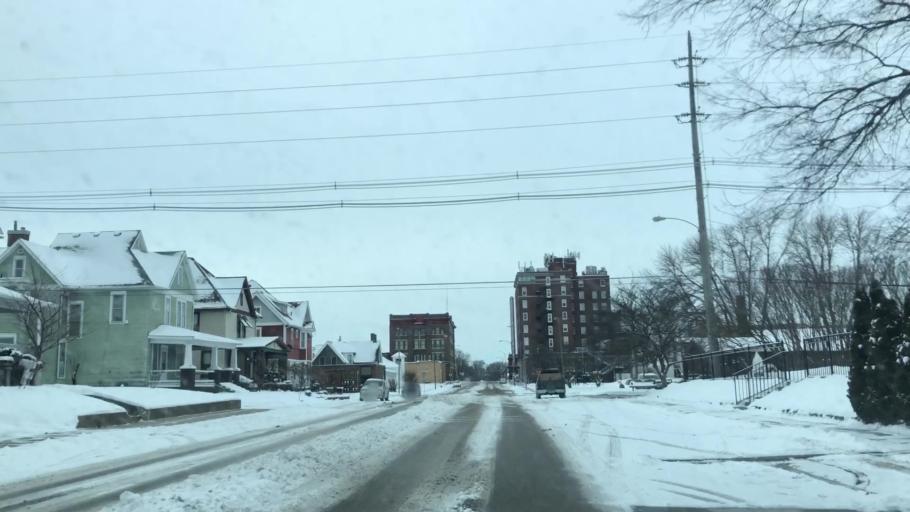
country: US
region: Iowa
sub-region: Marshall County
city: Marshalltown
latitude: 42.0514
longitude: -92.9097
